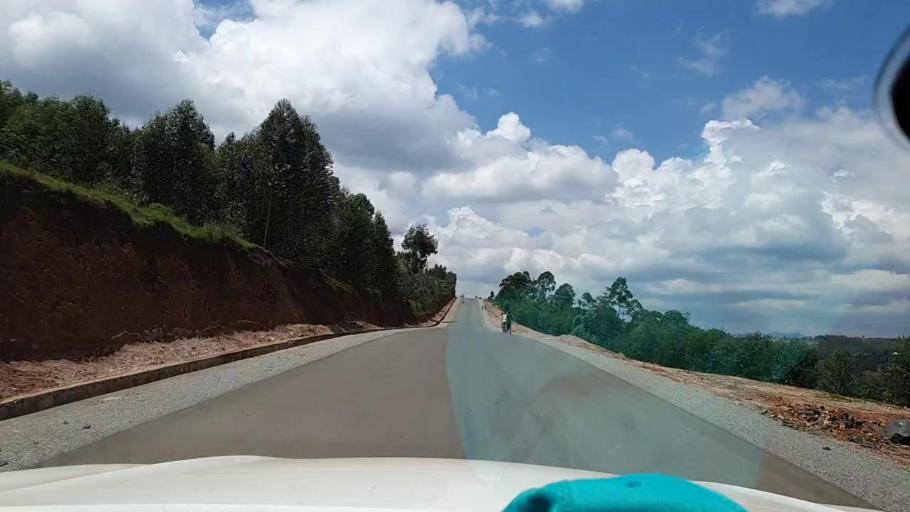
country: RW
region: Southern Province
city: Nzega
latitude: -2.6425
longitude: 29.5755
